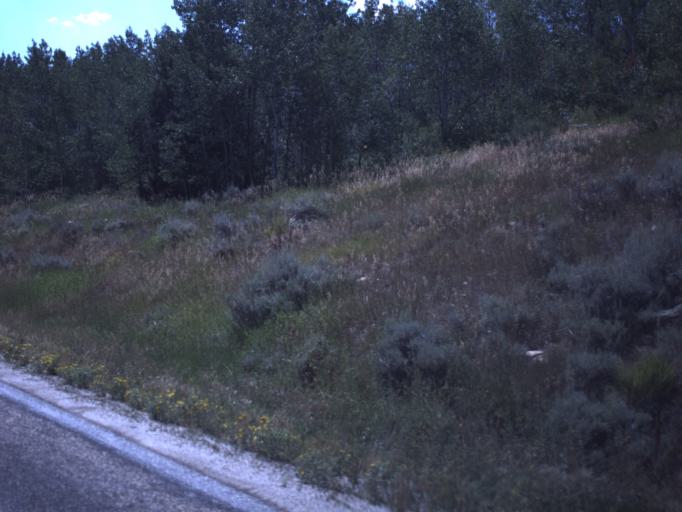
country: US
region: Utah
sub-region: Cache County
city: Richmond
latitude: 41.8736
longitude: -111.5661
